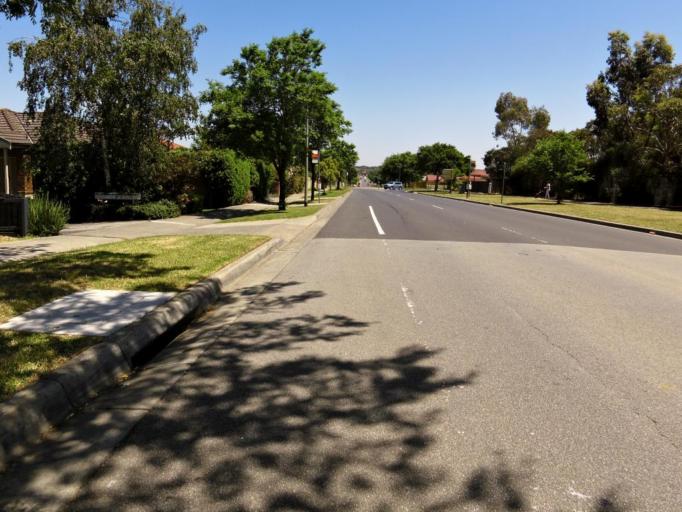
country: AU
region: Victoria
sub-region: Casey
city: Berwick
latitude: -38.0499
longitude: 145.3321
